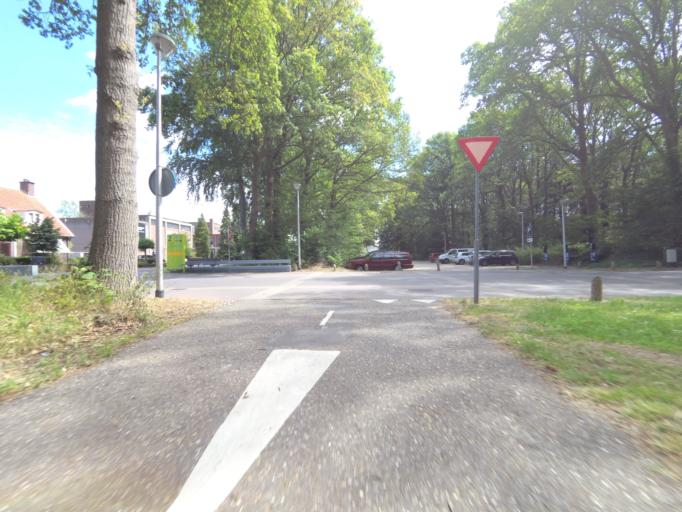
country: NL
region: Gelderland
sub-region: Gemeente Voorst
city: Wilp
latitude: 52.2171
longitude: 6.1403
